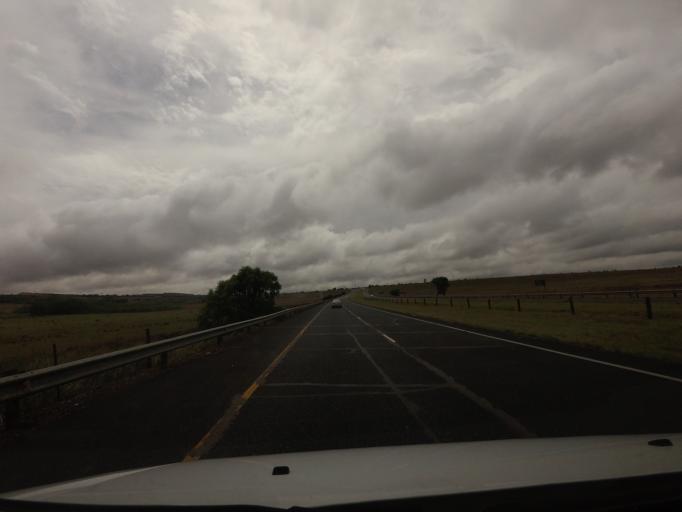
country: ZA
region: Mpumalanga
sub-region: Nkangala District Municipality
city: Middelburg
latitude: -25.8500
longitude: 29.3905
